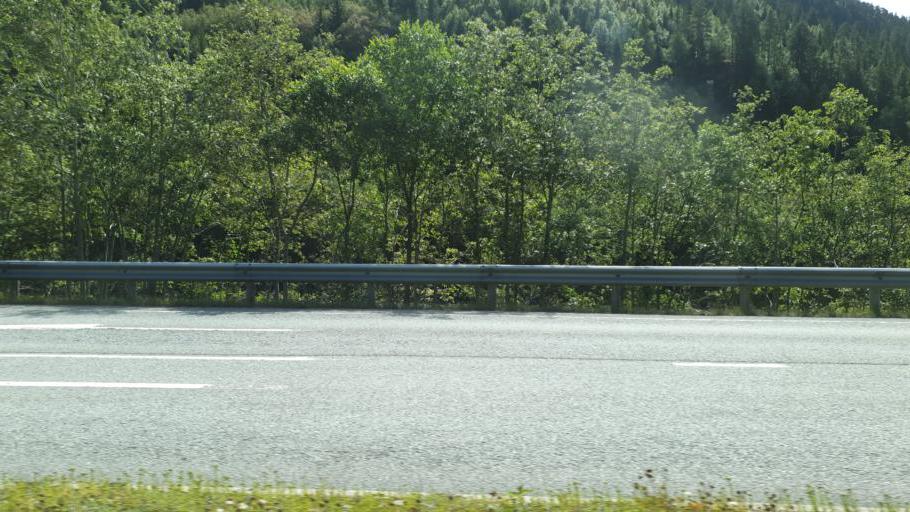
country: NO
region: Sor-Trondelag
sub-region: Midtre Gauldal
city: Storen
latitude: 63.0255
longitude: 10.2545
